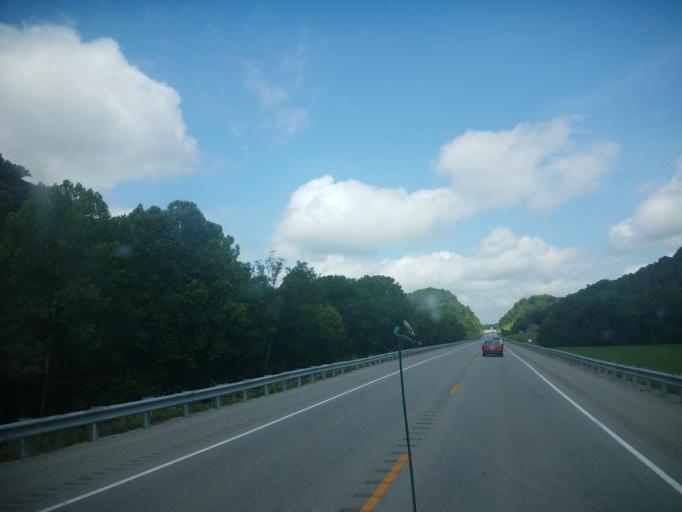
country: US
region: Kentucky
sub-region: Cumberland County
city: Burkesville
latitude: 36.7609
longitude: -85.3341
